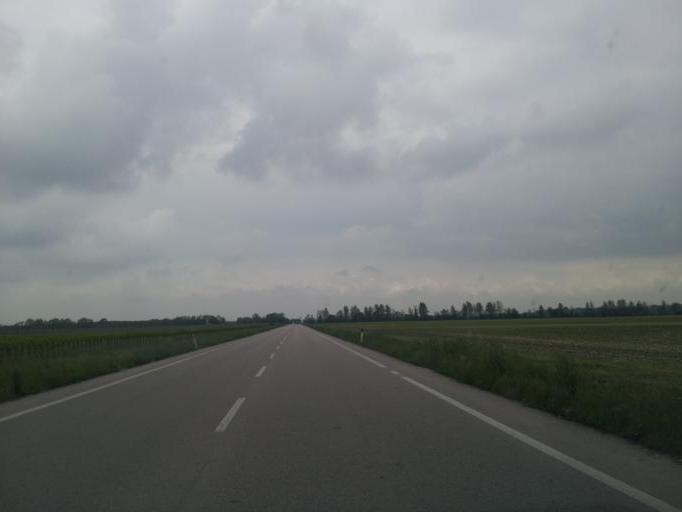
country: IT
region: Friuli Venezia Giulia
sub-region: Provincia di Udine
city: Varmo
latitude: 45.9249
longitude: 12.9873
